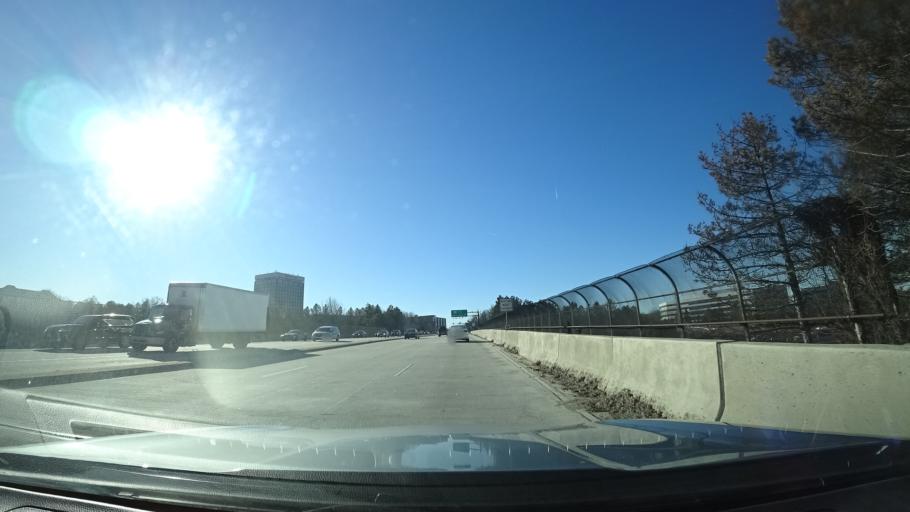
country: US
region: Virginia
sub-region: Fairfax County
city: Reston
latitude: 38.9529
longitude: -77.3562
